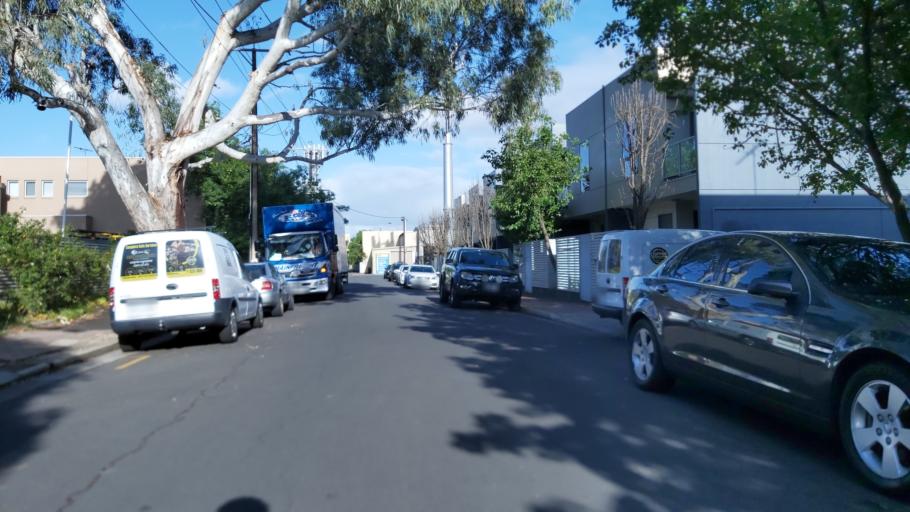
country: AU
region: South Australia
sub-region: Unley
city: Unley
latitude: -34.9476
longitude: 138.6047
